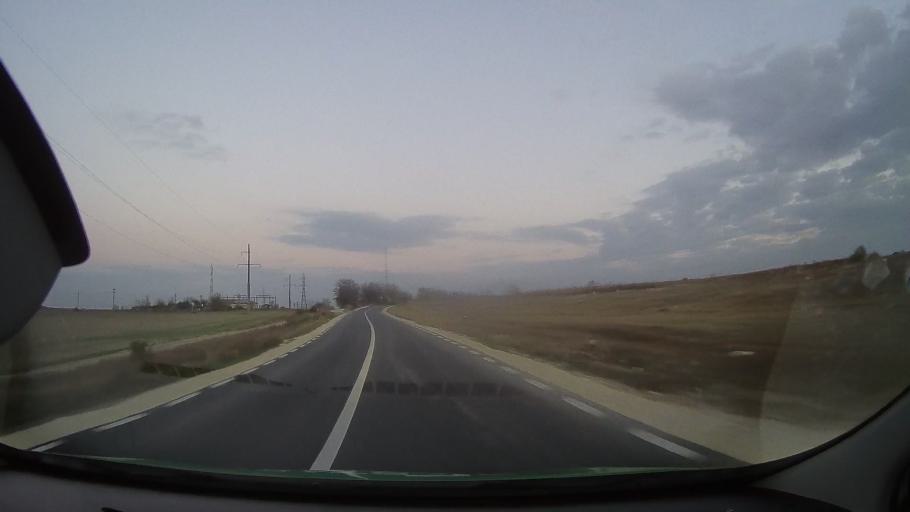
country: RO
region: Constanta
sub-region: Comuna Baneasa
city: Baneasa
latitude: 44.0800
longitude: 27.6906
